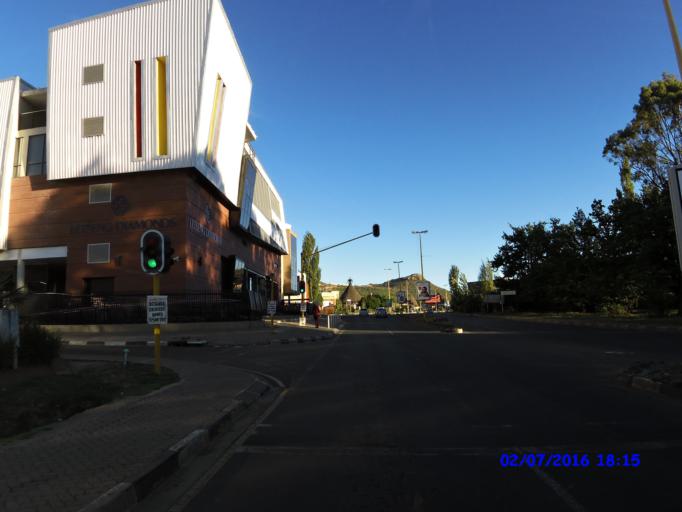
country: LS
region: Maseru
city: Maseru
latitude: -29.3110
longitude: 27.4763
